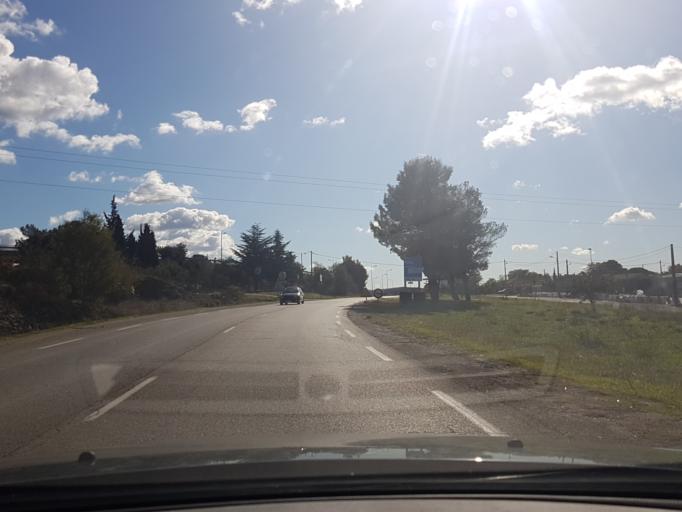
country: FR
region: Provence-Alpes-Cote d'Azur
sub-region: Departement du Vaucluse
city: Vedene
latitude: 43.9678
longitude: 4.8973
